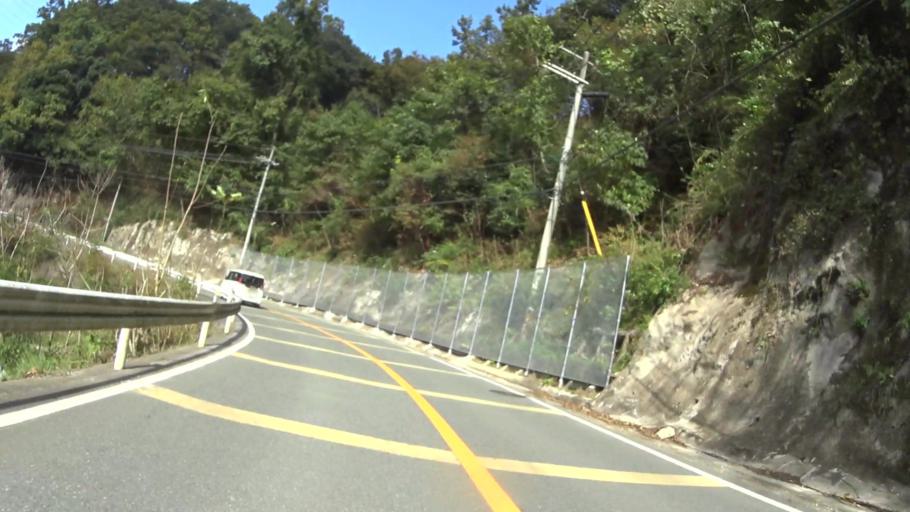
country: JP
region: Kyoto
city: Fukuchiyama
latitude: 35.3403
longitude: 135.0687
